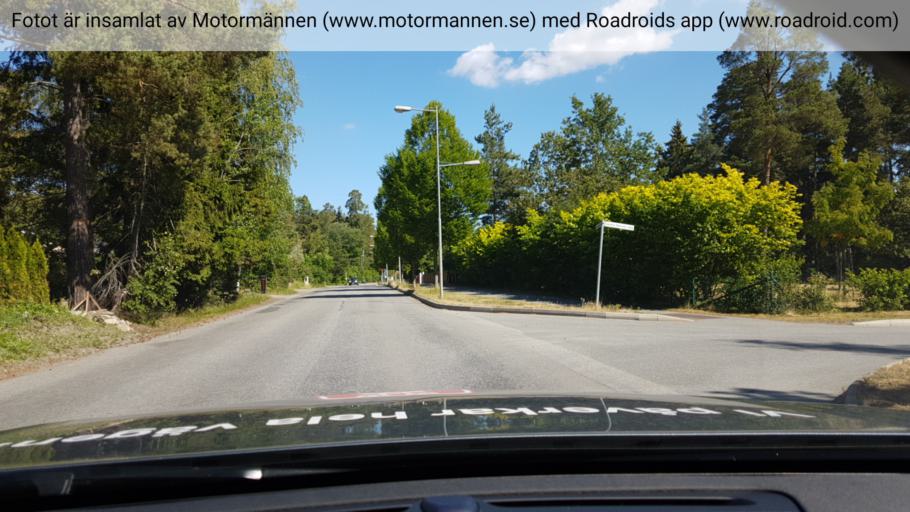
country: SE
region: Stockholm
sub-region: Nacka Kommun
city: Fisksatra
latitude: 59.2471
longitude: 18.2731
